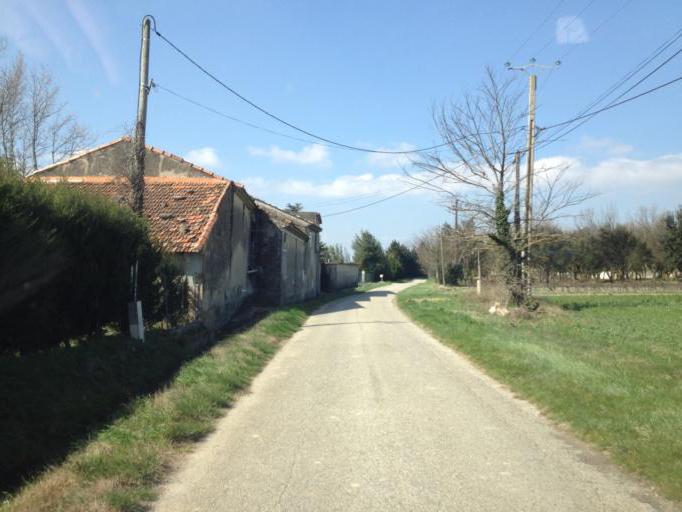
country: FR
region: Provence-Alpes-Cote d'Azur
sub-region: Departement du Vaucluse
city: Jonquieres
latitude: 44.1151
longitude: 4.9202
